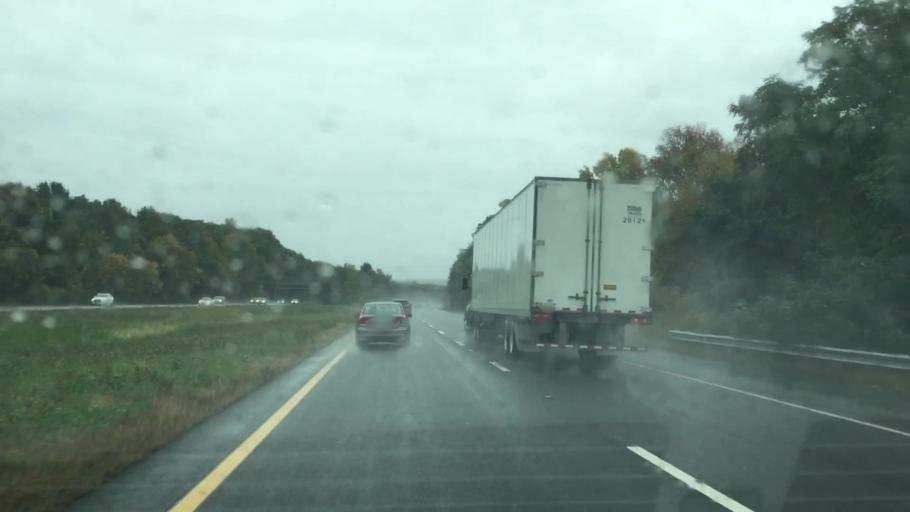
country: US
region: Massachusetts
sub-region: Essex County
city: Amesbury
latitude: 42.8489
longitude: -70.9146
